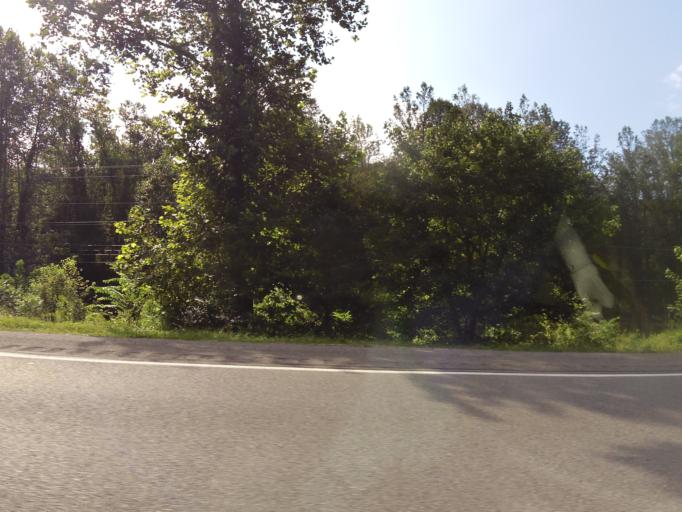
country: US
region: Kentucky
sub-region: Bell County
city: Pineville
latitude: 36.7067
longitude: -83.6968
